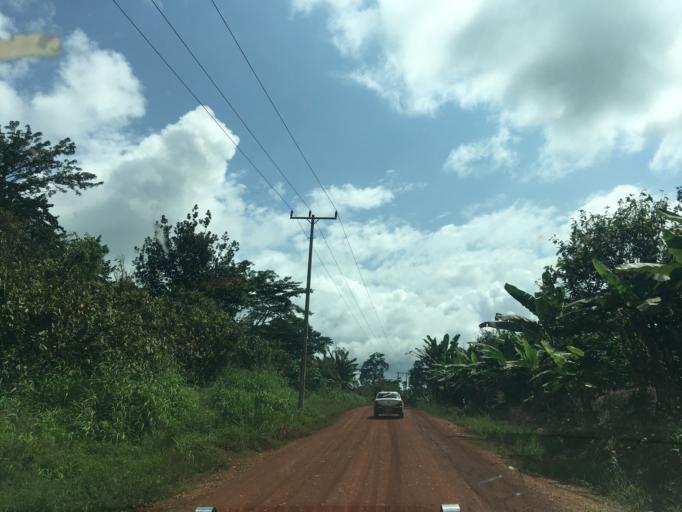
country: GH
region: Western
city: Wassa-Akropong
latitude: 5.7832
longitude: -2.3914
